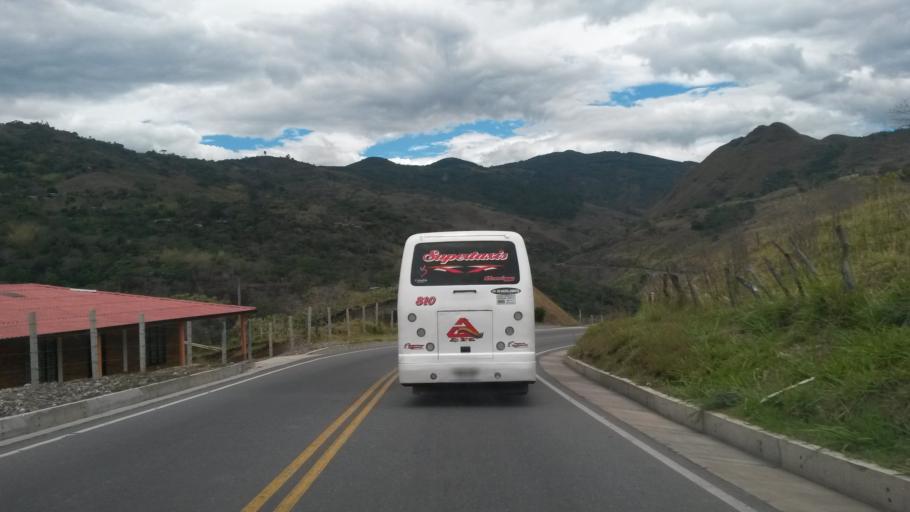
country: CO
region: Cauca
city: Rosas
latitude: 2.2820
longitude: -76.7170
